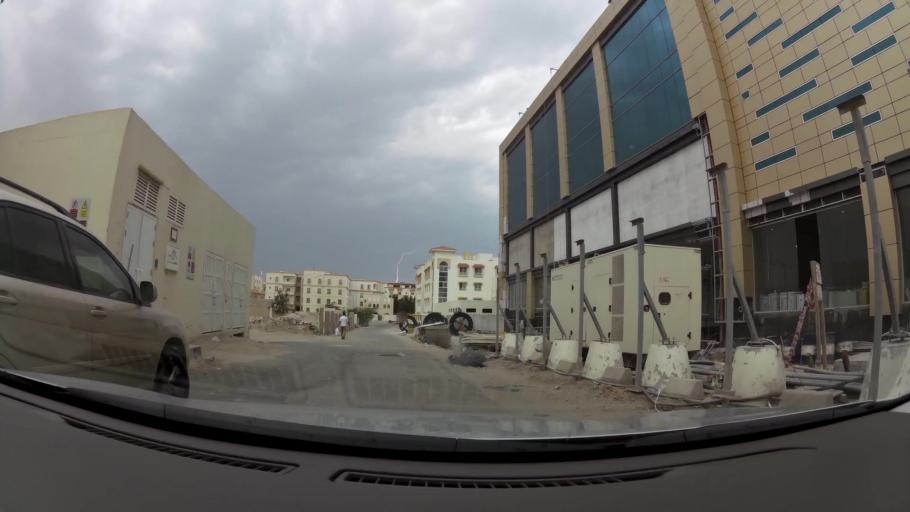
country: QA
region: Baladiyat ad Dawhah
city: Doha
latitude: 25.2737
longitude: 51.4965
